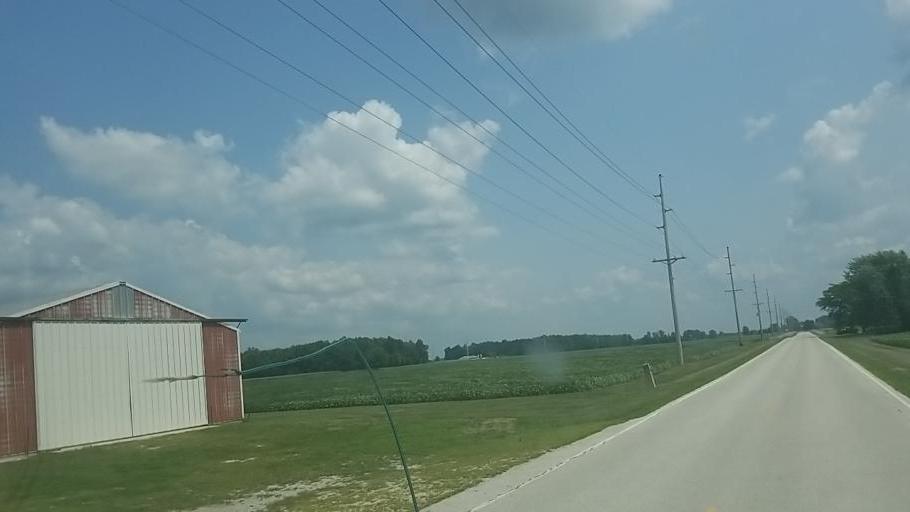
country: US
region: Ohio
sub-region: Wyandot County
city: Carey
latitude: 40.9635
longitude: -83.3150
